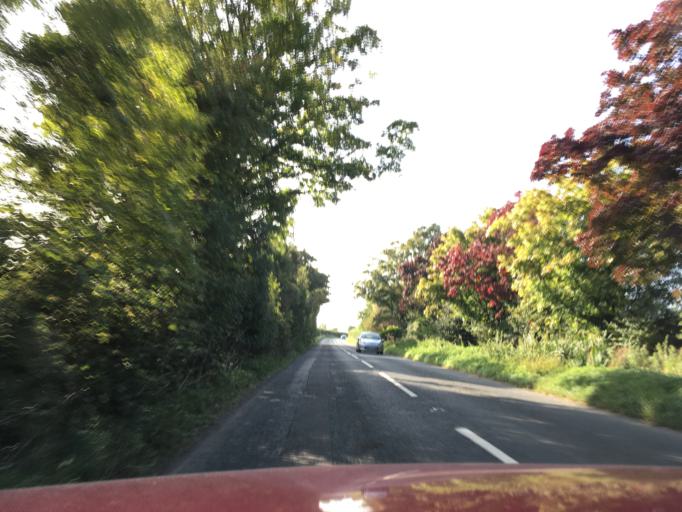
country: GB
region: England
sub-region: Gloucestershire
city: Tewkesbury
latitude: 51.9585
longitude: -2.2464
